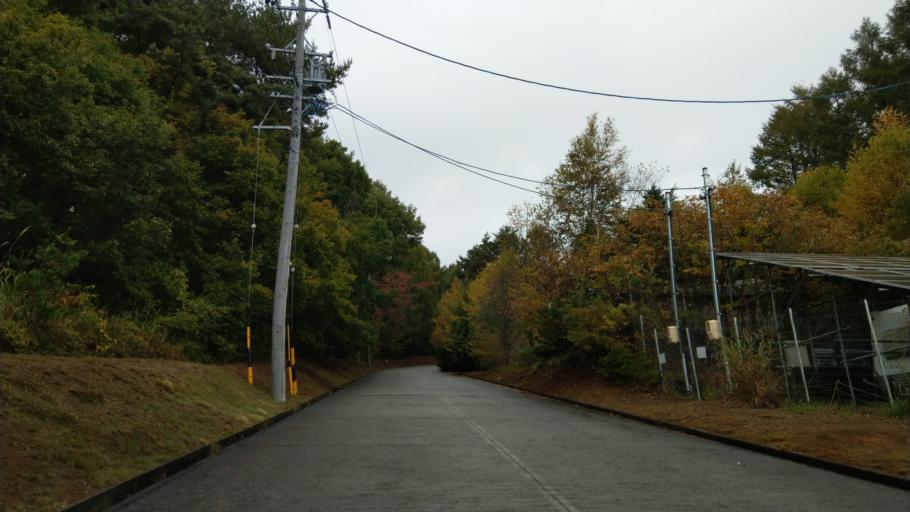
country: JP
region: Nagano
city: Komoro
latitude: 36.3651
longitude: 138.4266
